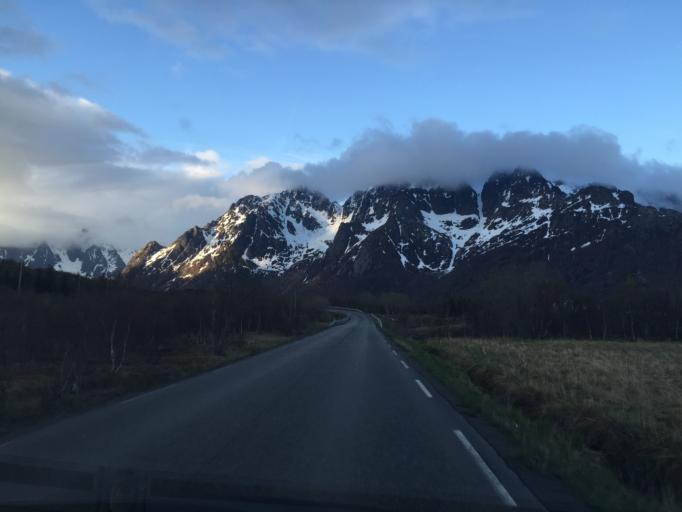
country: NO
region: Nordland
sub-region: Vagan
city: Svolvaer
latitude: 68.2863
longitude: 14.6883
